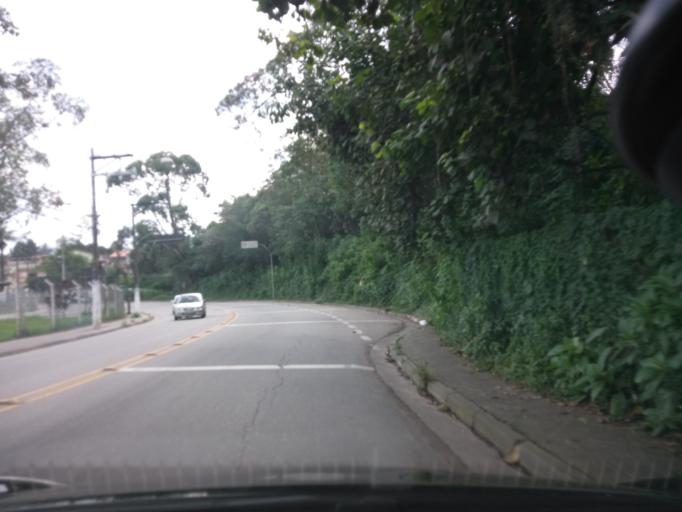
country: BR
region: Sao Paulo
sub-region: Sao Bernardo Do Campo
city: Sao Bernardo do Campo
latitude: -23.7428
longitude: -46.5811
